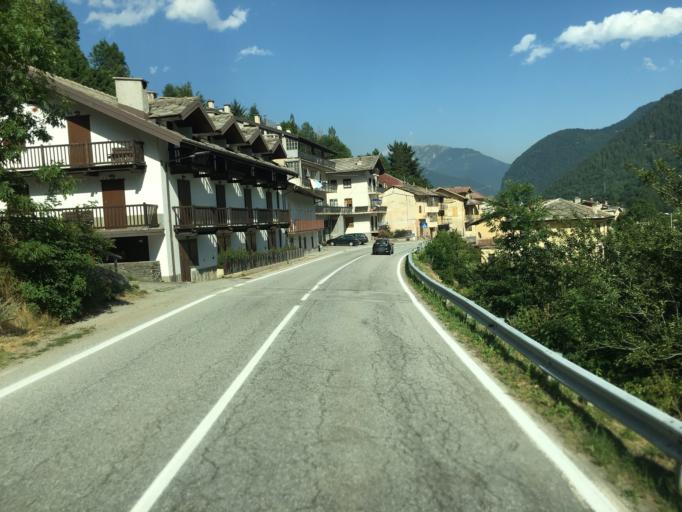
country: IT
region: Piedmont
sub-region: Provincia di Torino
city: Fenestrelle
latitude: 45.0270
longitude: 7.0657
